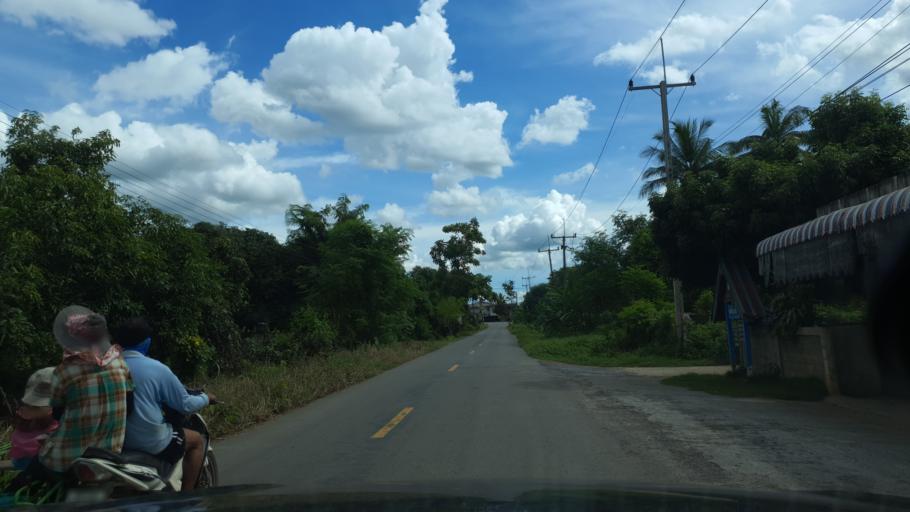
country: TH
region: Sukhothai
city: Thung Saliam
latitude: 17.3280
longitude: 99.6313
